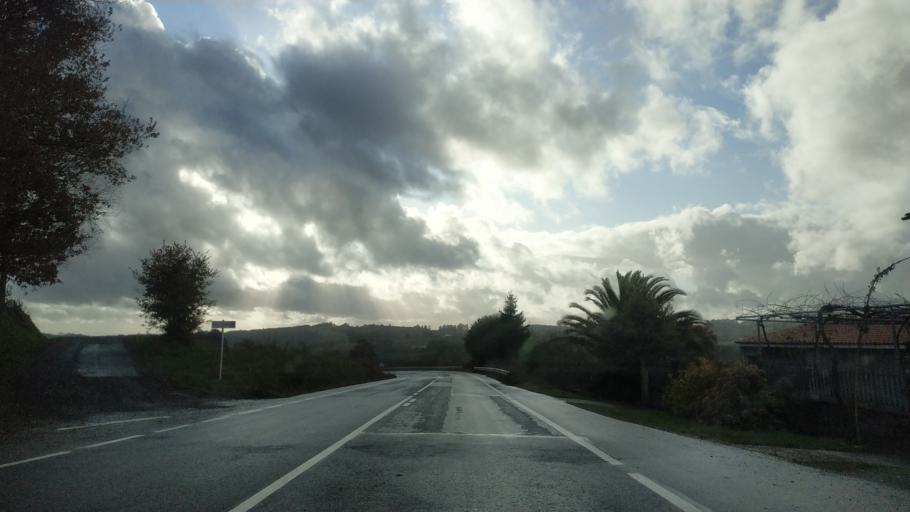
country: ES
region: Galicia
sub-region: Provincia da Coruna
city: Boimorto
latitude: 42.9688
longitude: -8.1414
